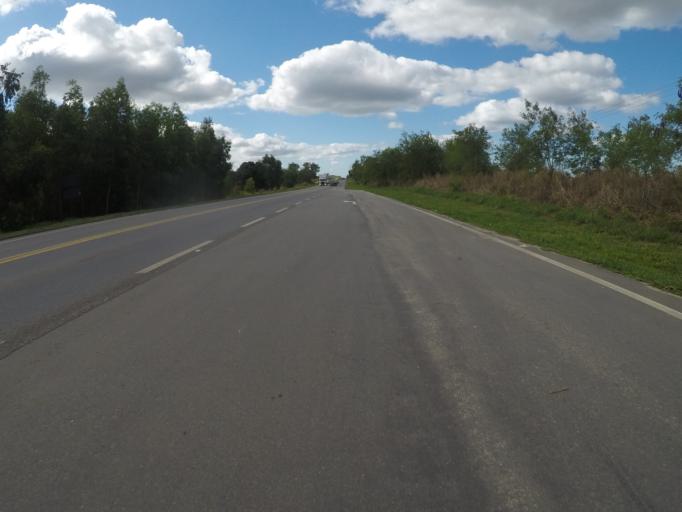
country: BR
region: Espirito Santo
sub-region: Linhares
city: Linhares
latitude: -19.1765
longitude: -40.0911
